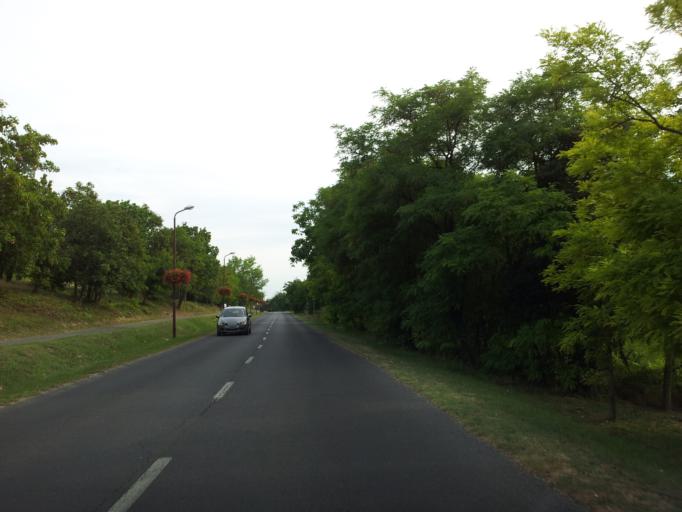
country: HU
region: Veszprem
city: Tihany
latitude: 46.9051
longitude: 17.8904
